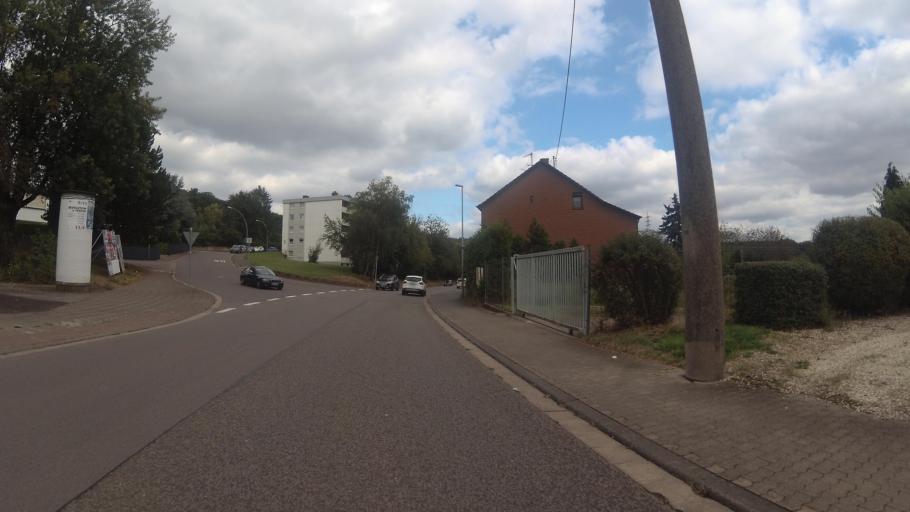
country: DE
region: Saarland
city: Puttlingen
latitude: 49.2588
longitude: 6.8891
